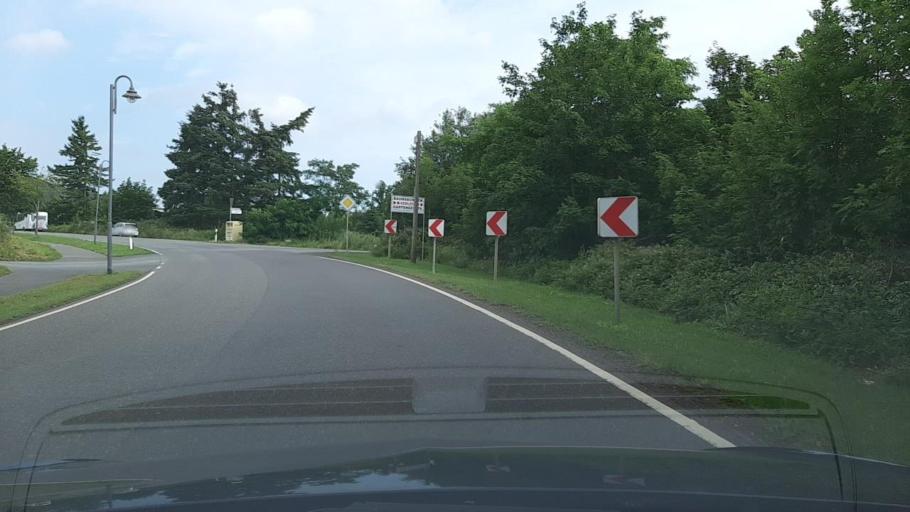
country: DE
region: Rheinland-Pfalz
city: Mendig
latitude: 50.3787
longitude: 7.2811
